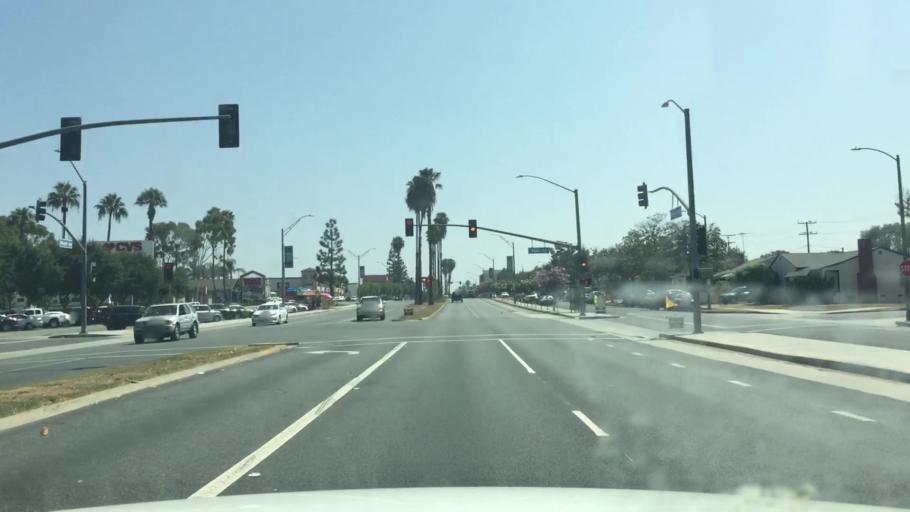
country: US
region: California
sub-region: Los Angeles County
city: Signal Hill
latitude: 33.8430
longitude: -118.1850
